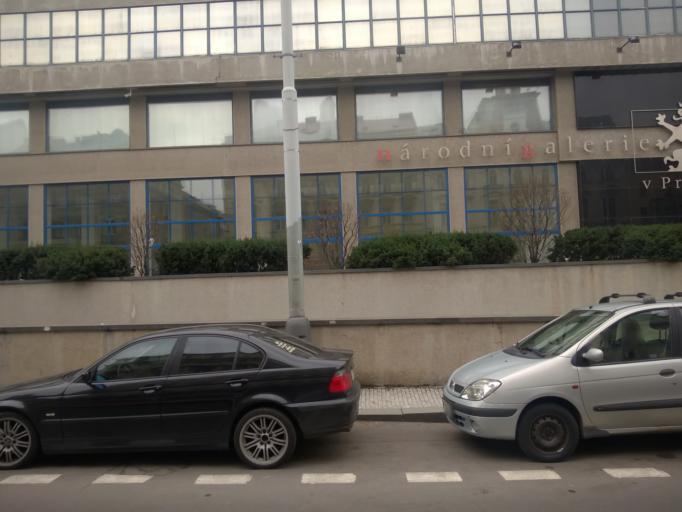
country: CZ
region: Praha
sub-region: Praha 8
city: Karlin
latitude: 50.1015
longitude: 14.4331
